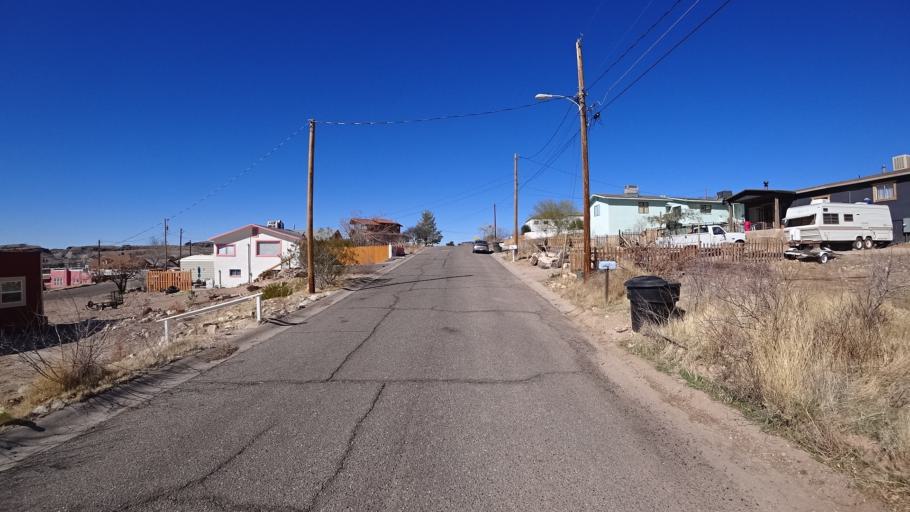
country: US
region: Arizona
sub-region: Mohave County
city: Kingman
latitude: 35.1953
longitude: -114.0565
